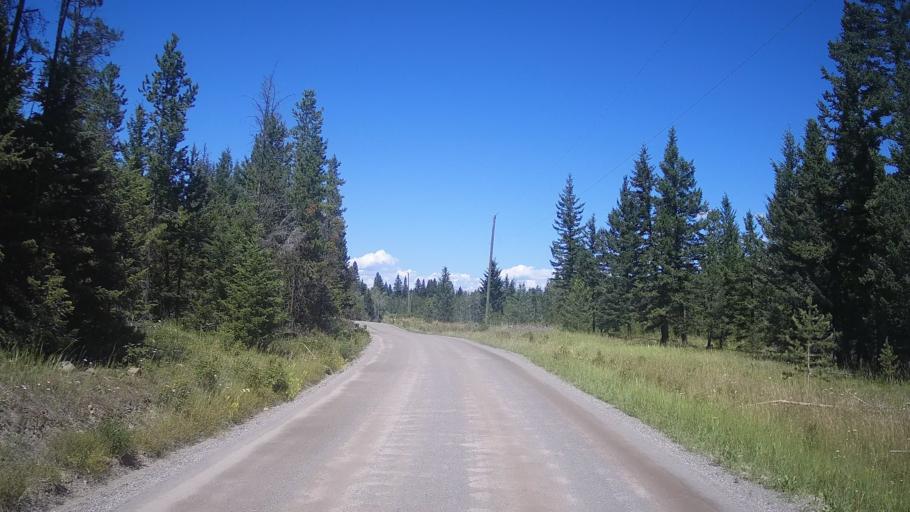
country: CA
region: British Columbia
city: Cache Creek
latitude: 51.1989
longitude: -121.5910
